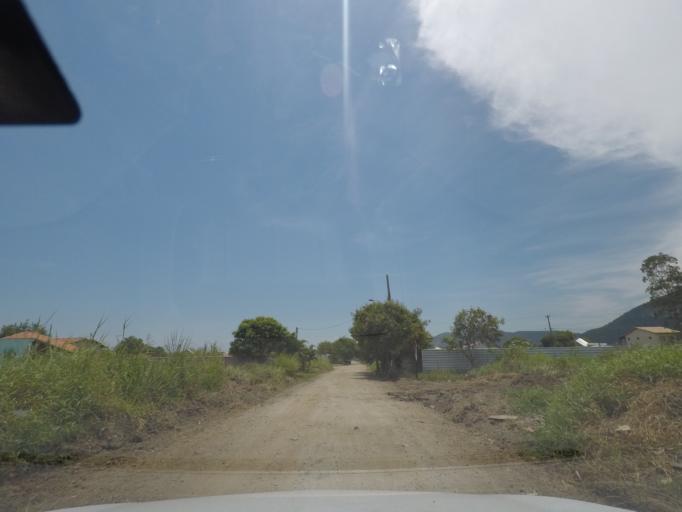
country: BR
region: Rio de Janeiro
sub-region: Marica
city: Marica
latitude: -22.9543
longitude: -42.9488
